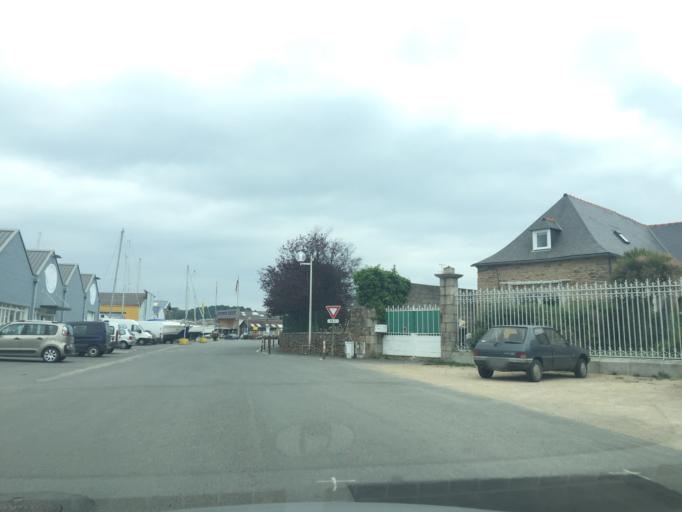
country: FR
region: Brittany
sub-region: Departement des Cotes-d'Armor
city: Paimpol
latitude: 48.7811
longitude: -3.0424
